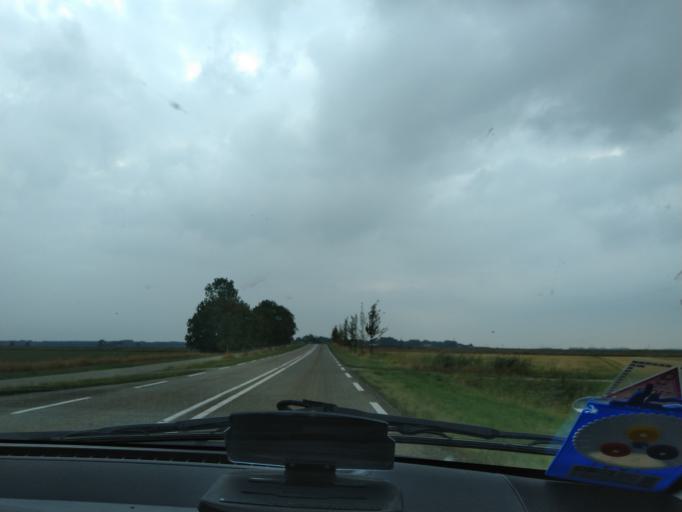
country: NL
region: Groningen
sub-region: Gemeente Vlagtwedde
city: Vlagtwedde
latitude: 53.1083
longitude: 7.1116
